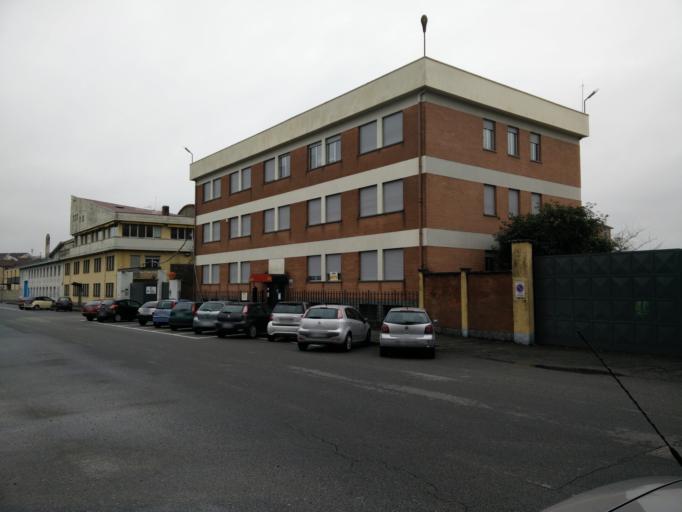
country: IT
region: Piedmont
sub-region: Provincia di Torino
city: Nichelino
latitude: 45.0197
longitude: 7.6500
